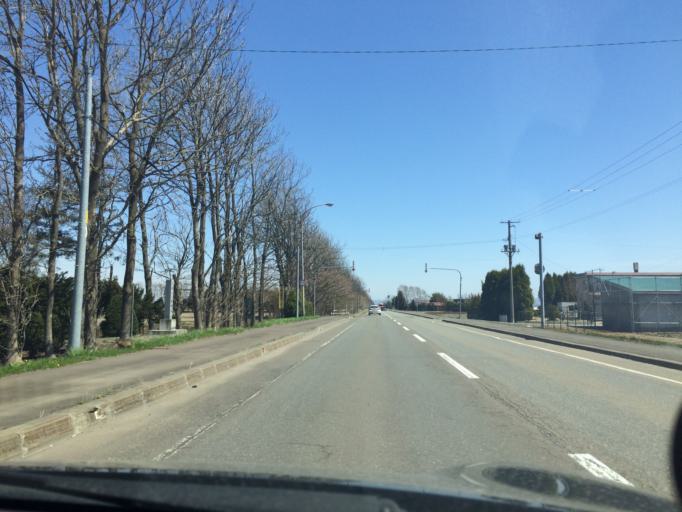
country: JP
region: Hokkaido
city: Kitahiroshima
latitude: 43.0290
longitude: 141.5978
